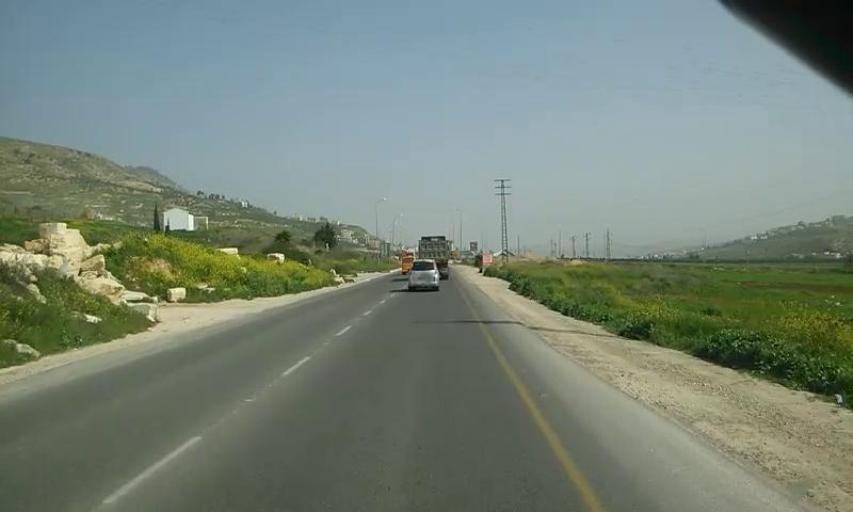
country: PS
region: West Bank
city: `Awarta
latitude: 32.1746
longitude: 35.2716
